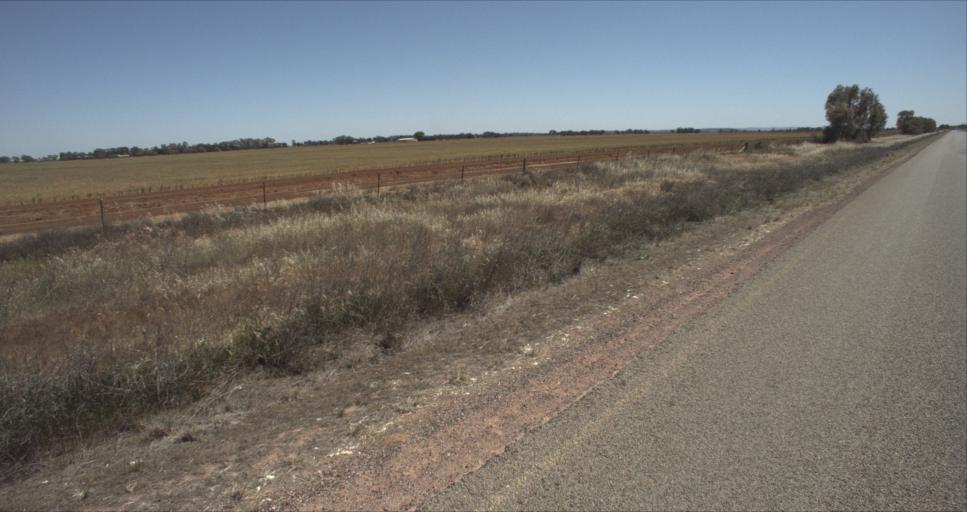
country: AU
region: New South Wales
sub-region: Leeton
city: Leeton
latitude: -34.4637
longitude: 146.2937
